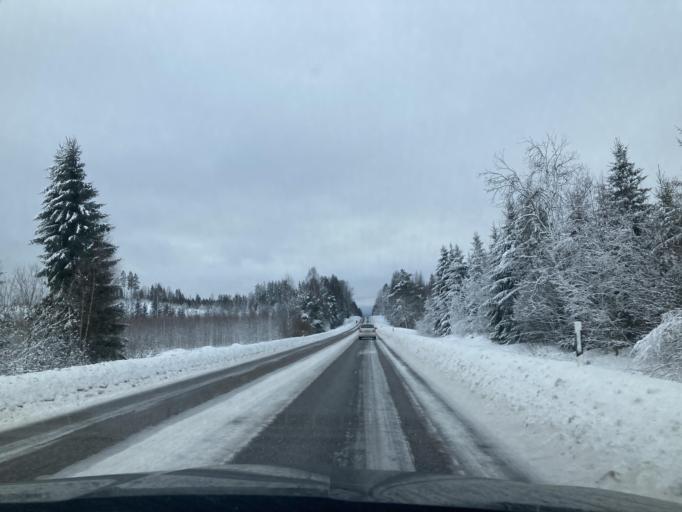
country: FI
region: Central Finland
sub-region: Jaemsae
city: Kuhmoinen
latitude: 61.5257
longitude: 25.1524
